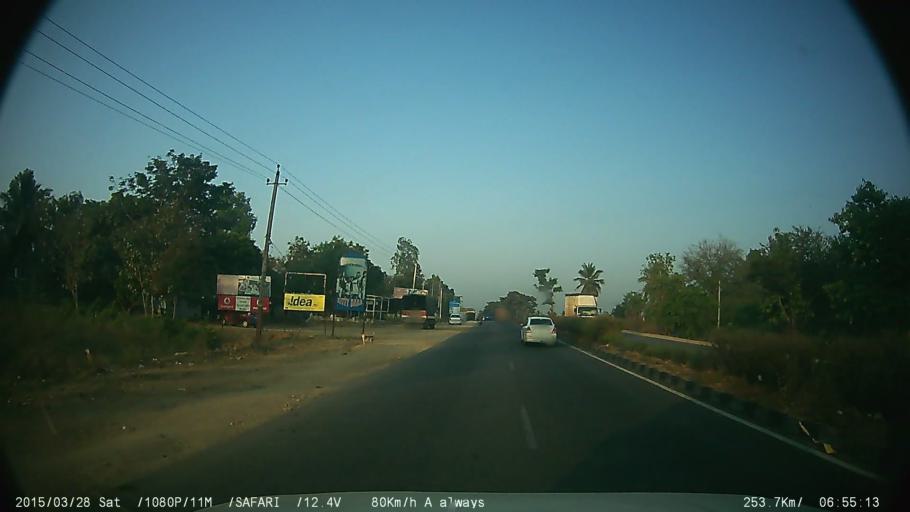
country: IN
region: Karnataka
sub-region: Mandya
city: Maddur
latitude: 12.5755
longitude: 77.0184
